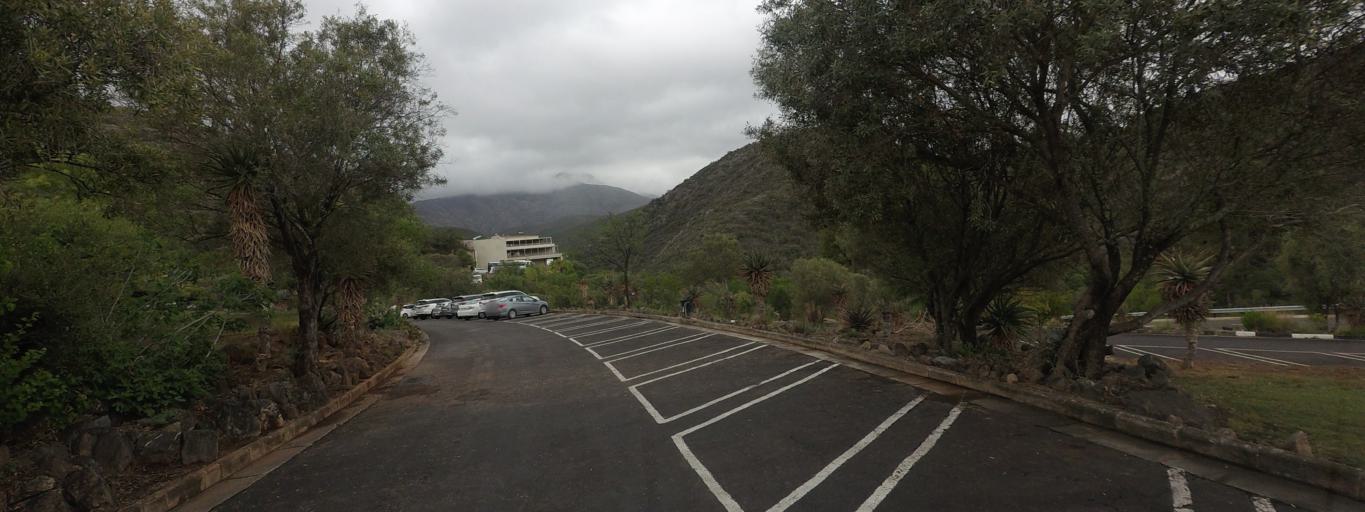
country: ZA
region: Western Cape
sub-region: Eden District Municipality
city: Oudtshoorn
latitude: -33.3943
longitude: 22.2148
